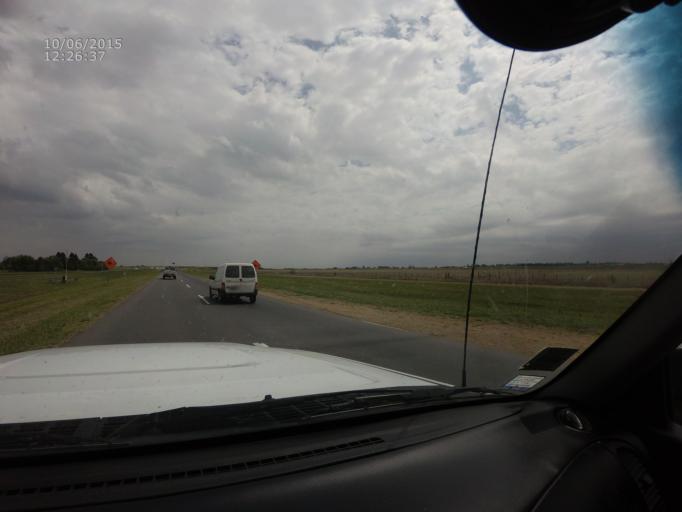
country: AR
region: Santa Fe
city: Roldan
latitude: -32.9026
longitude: -61.0226
